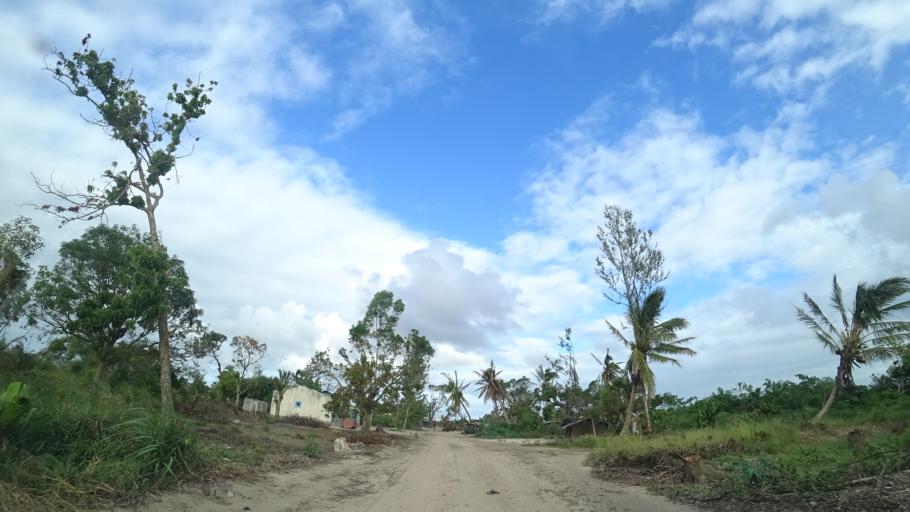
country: MZ
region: Sofala
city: Beira
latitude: -19.6522
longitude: 35.0589
